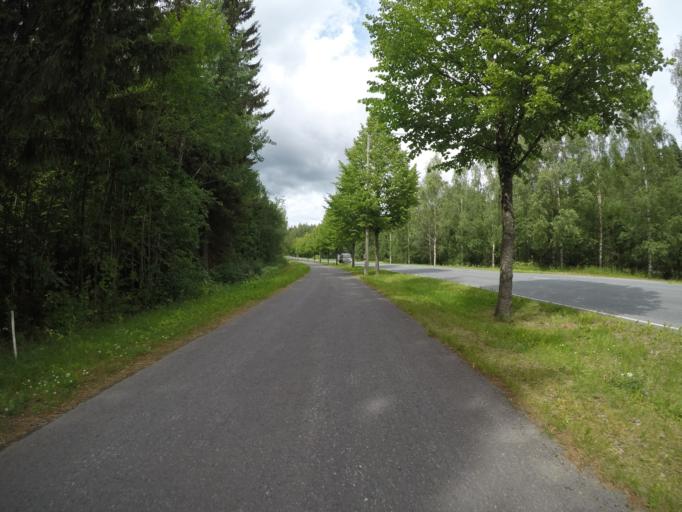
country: FI
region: Haeme
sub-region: Haemeenlinna
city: Haemeenlinna
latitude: 60.9664
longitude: 24.4455
